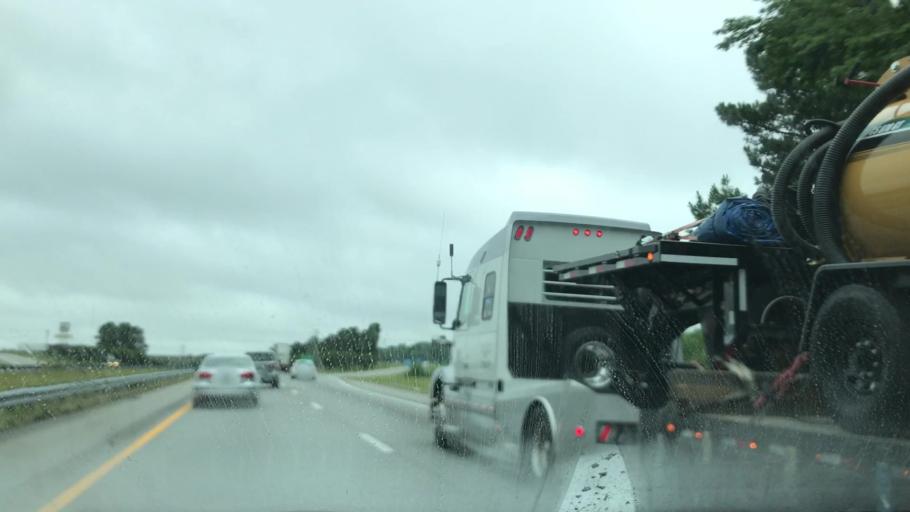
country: US
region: North Carolina
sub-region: Halifax County
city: Halifax
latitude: 36.3611
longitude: -77.6747
